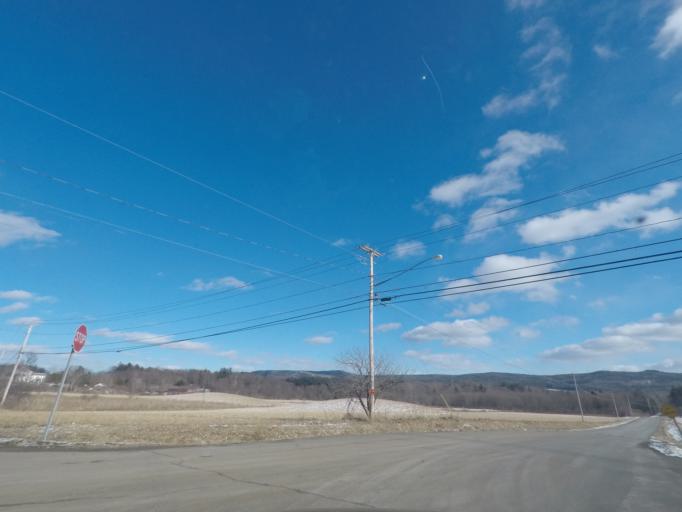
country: US
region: New York
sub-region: Rensselaer County
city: Poestenkill
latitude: 42.8048
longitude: -73.5514
